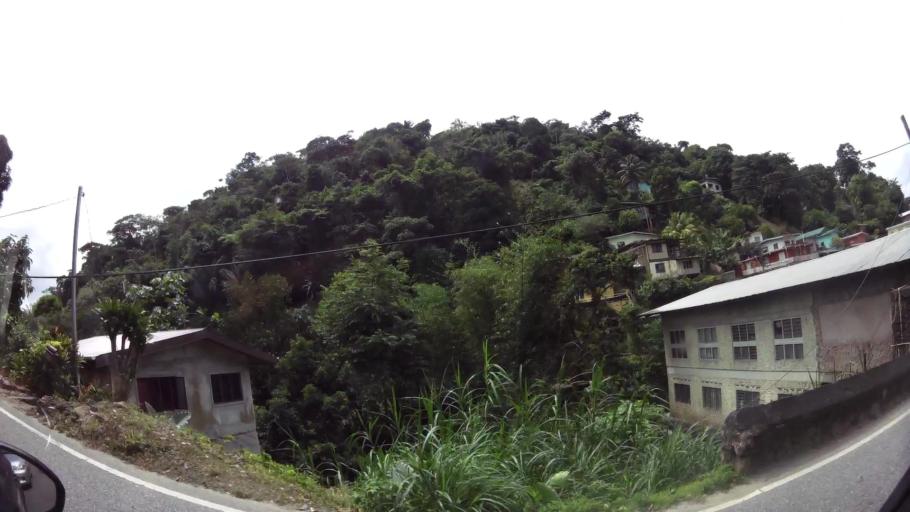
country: TT
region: Diego Martin
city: Petit Valley
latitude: 10.7148
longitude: -61.5258
